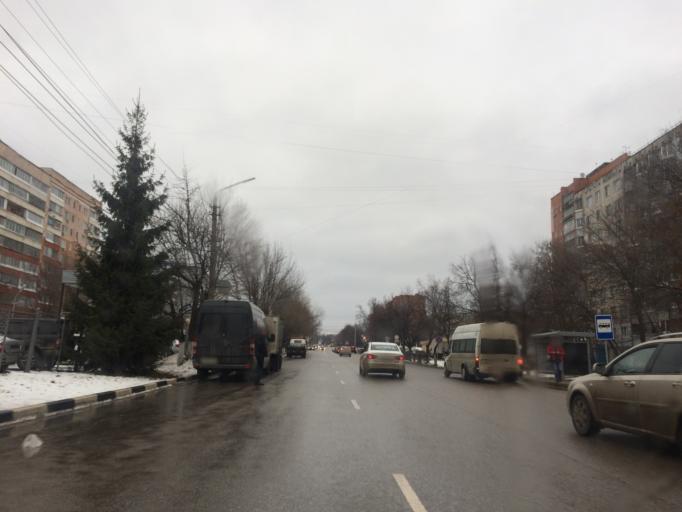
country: RU
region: Tula
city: Tula
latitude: 54.1989
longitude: 37.6476
